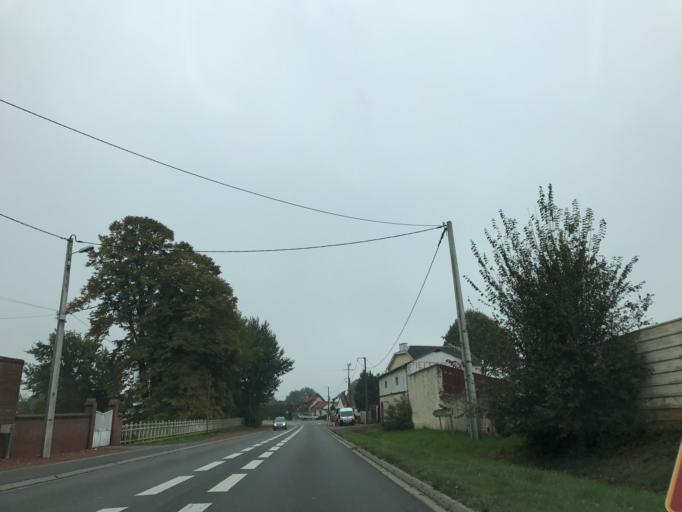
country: FR
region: Nord-Pas-de-Calais
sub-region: Departement du Pas-de-Calais
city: Beaurains
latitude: 50.2060
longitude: 2.8123
